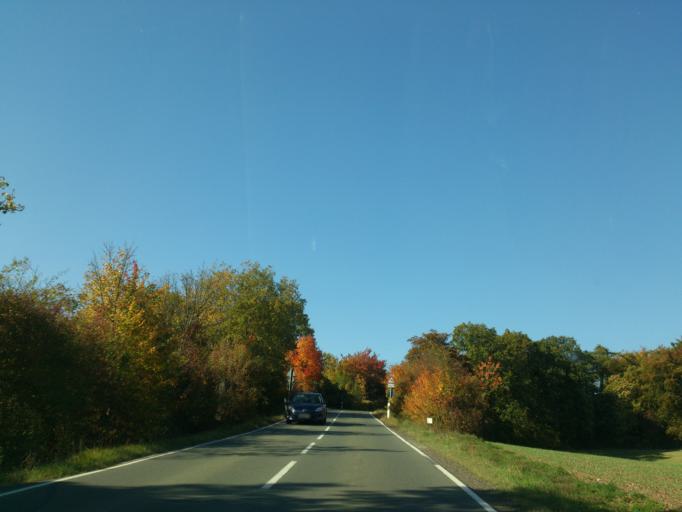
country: DE
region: Hesse
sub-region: Regierungsbezirk Kassel
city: Calden
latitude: 51.3754
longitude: 9.4173
